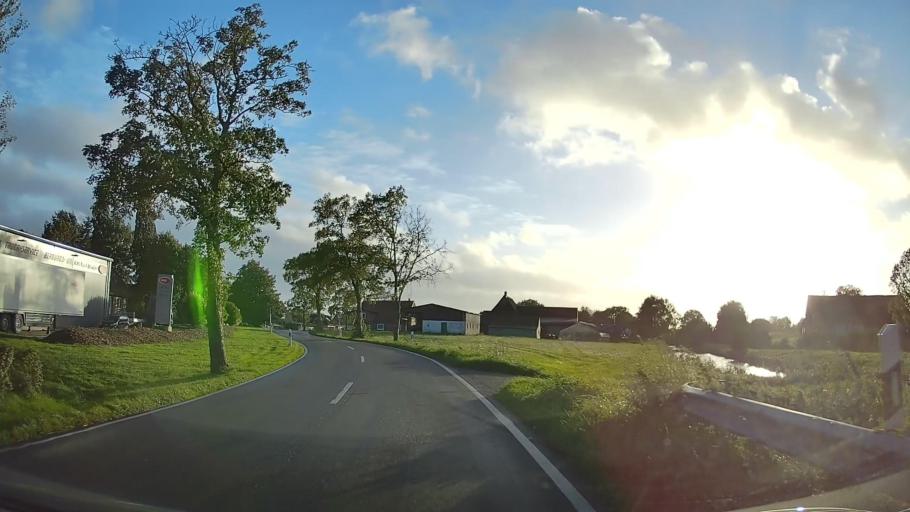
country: DE
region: Schleswig-Holstein
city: Herzhorn
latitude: 53.7930
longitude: 9.4924
